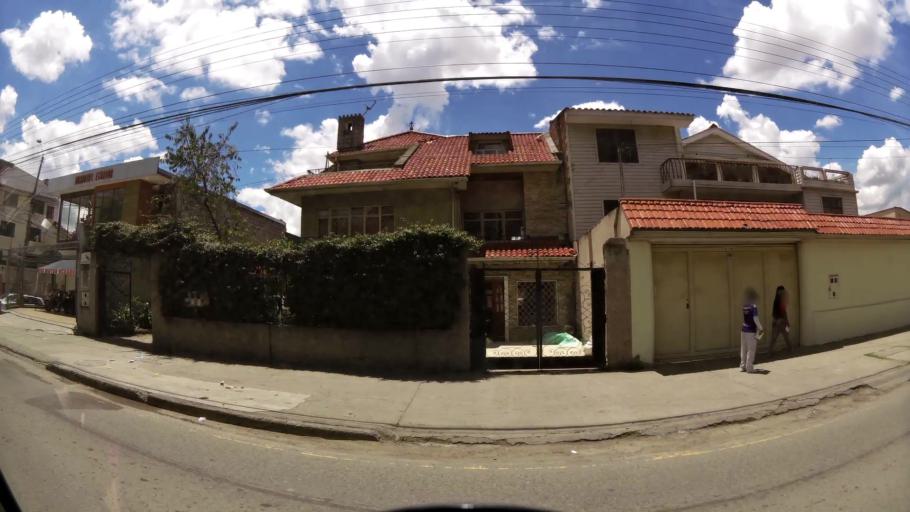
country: EC
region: Azuay
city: Cuenca
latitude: -2.8888
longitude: -79.0167
